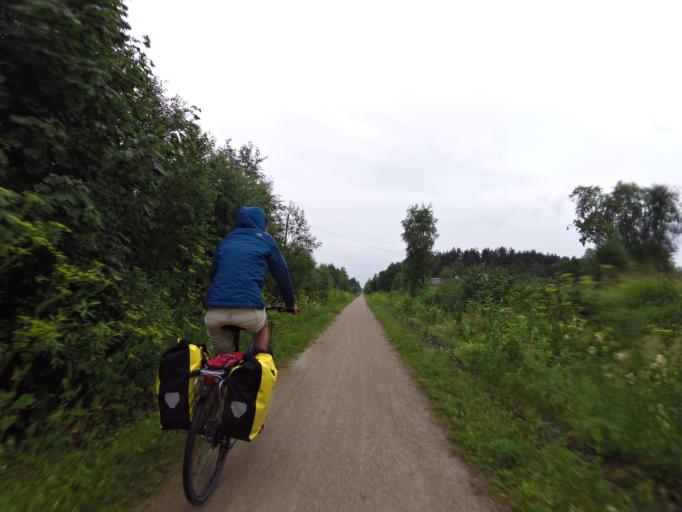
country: EE
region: Laeaene
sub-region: Lihula vald
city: Lihula
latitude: 58.9724
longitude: 23.8966
